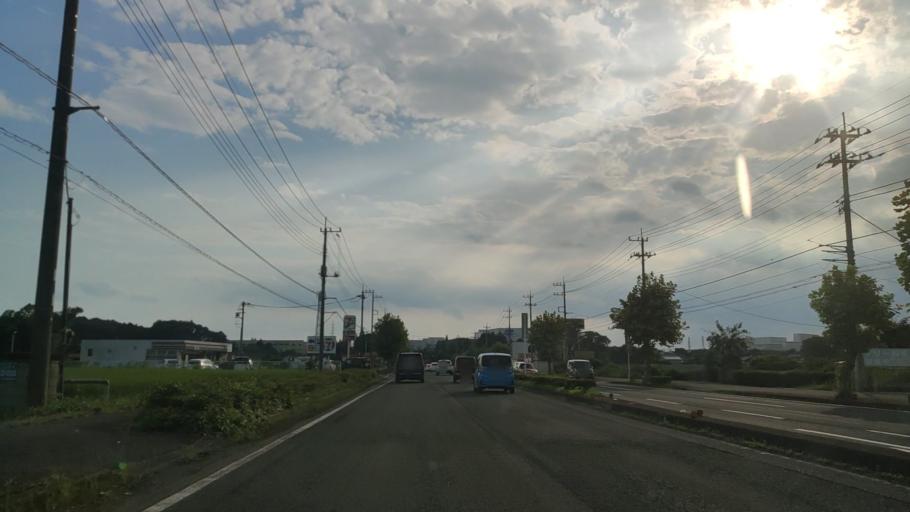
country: JP
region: Tochigi
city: Utsunomiya-shi
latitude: 36.5416
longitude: 139.8164
